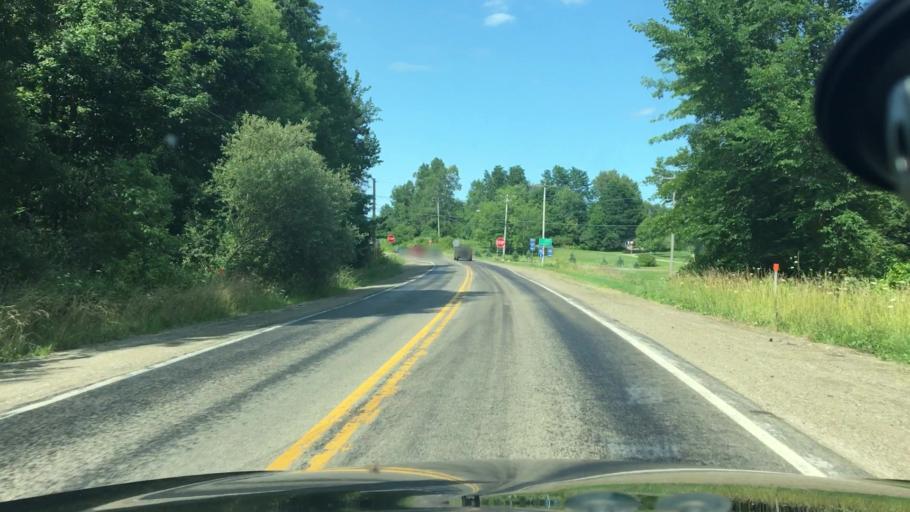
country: US
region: New York
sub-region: Chautauqua County
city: Lakewood
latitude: 42.2579
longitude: -79.3489
